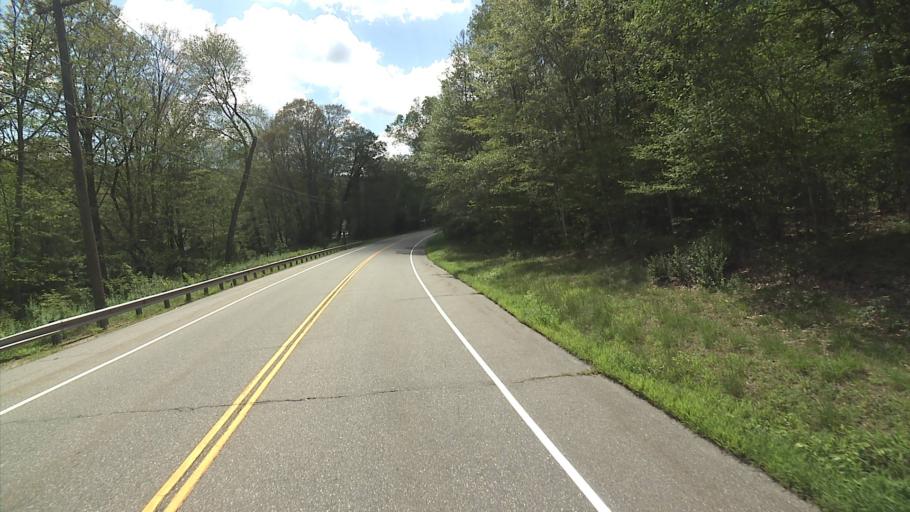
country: US
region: Connecticut
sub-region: Windham County
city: South Woodstock
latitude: 41.8599
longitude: -72.0914
